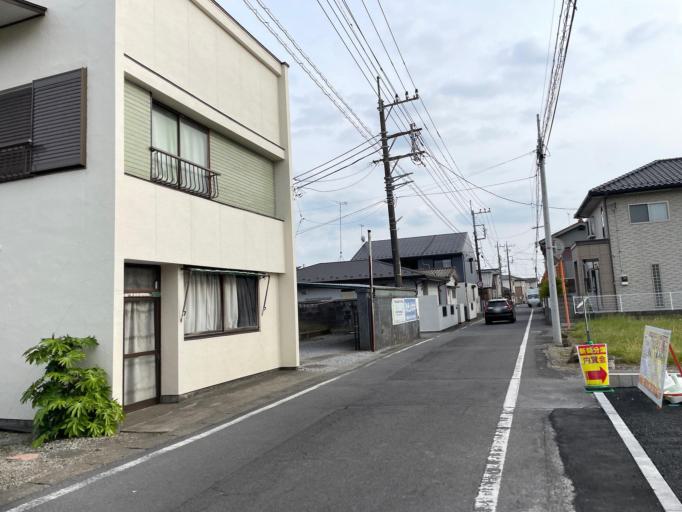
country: JP
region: Tochigi
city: Mibu
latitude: 36.4248
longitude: 139.8058
